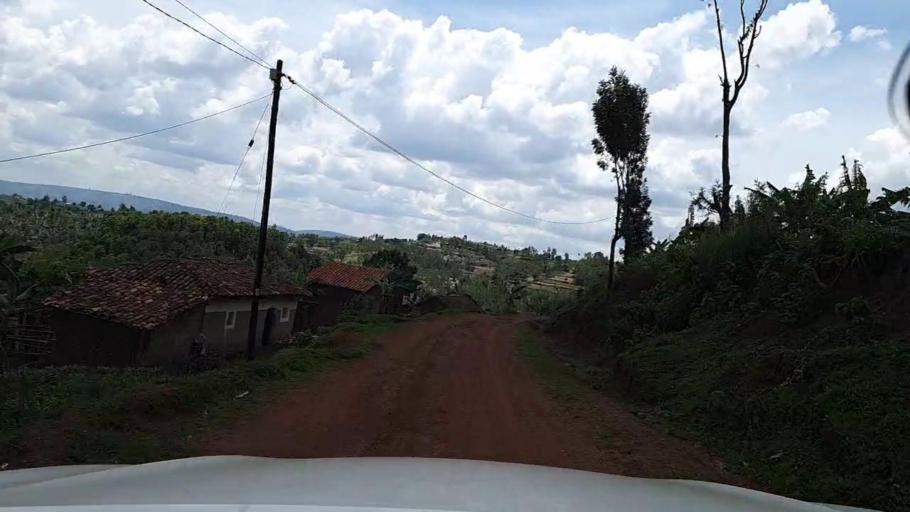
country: RW
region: Southern Province
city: Butare
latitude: -2.7594
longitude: 29.7471
